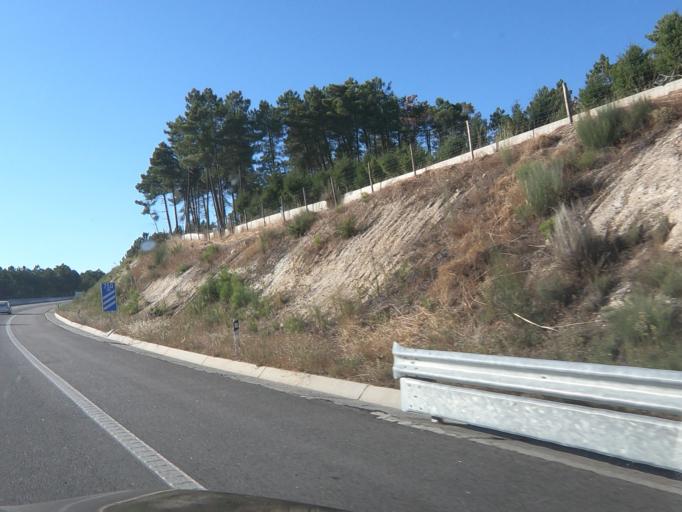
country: PT
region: Vila Real
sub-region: Murca
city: Murca
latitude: 41.3796
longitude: -7.5011
